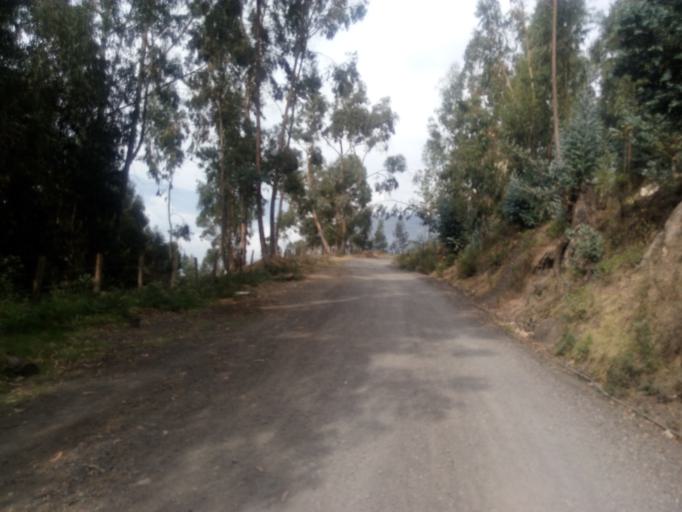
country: CO
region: Boyaca
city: Chita
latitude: 6.1923
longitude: -72.4762
